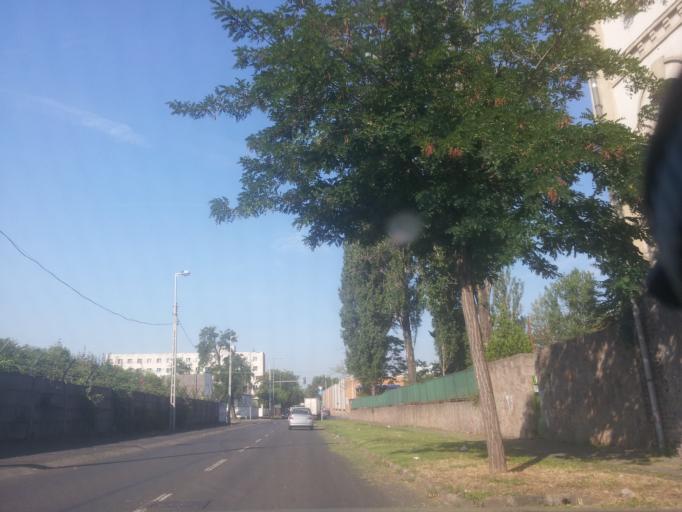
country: HU
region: Budapest
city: Budapest IX. keruelet
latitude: 47.4665
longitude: 19.0825
